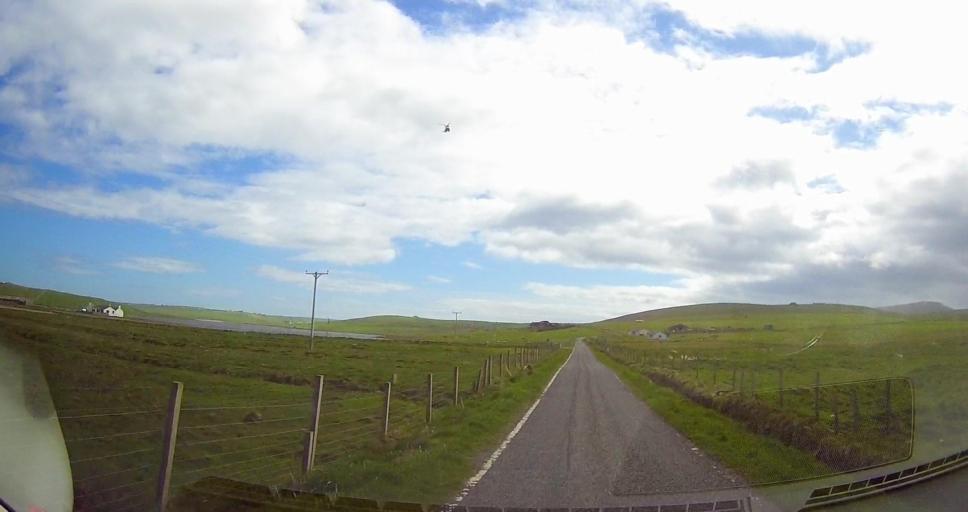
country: GB
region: Scotland
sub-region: Shetland Islands
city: Sandwick
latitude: 59.9372
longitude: -1.3460
